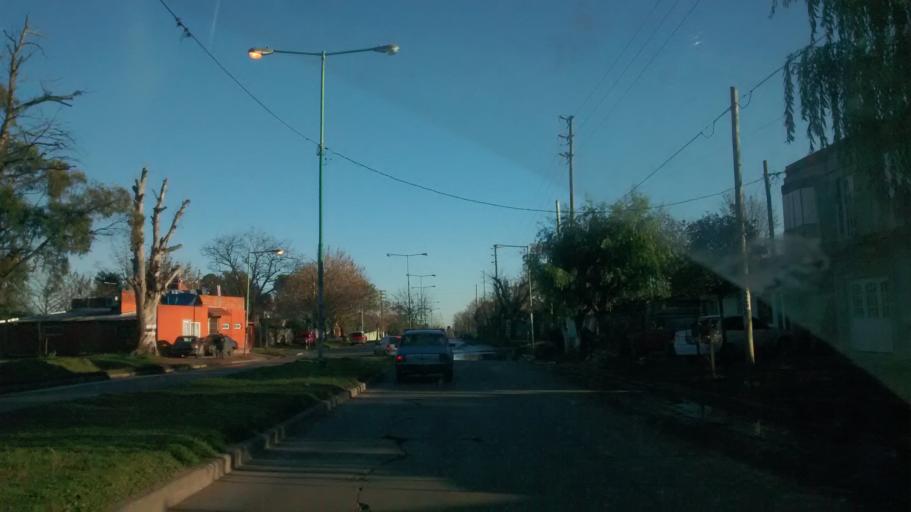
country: AR
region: Buenos Aires
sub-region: Partido de La Plata
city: La Plata
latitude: -34.9533
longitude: -57.9813
